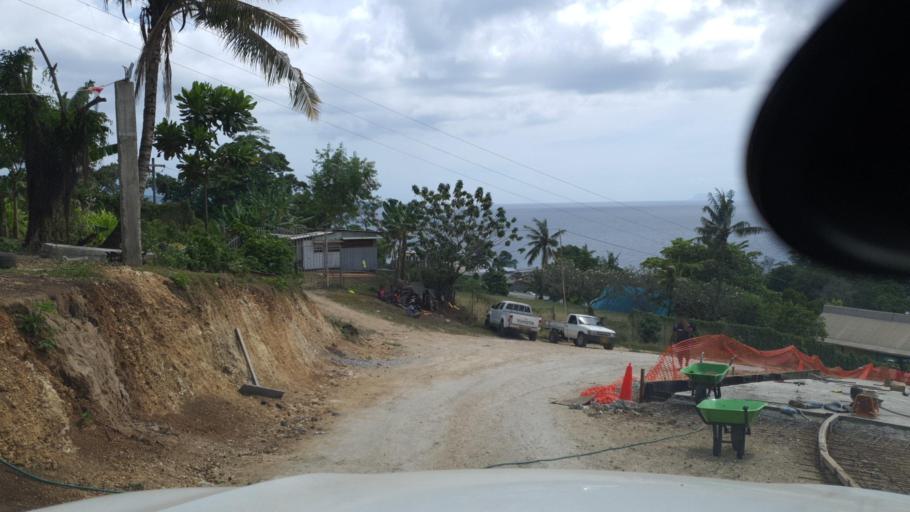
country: SB
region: Guadalcanal
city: Honiara
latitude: -9.4261
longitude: 159.9246
